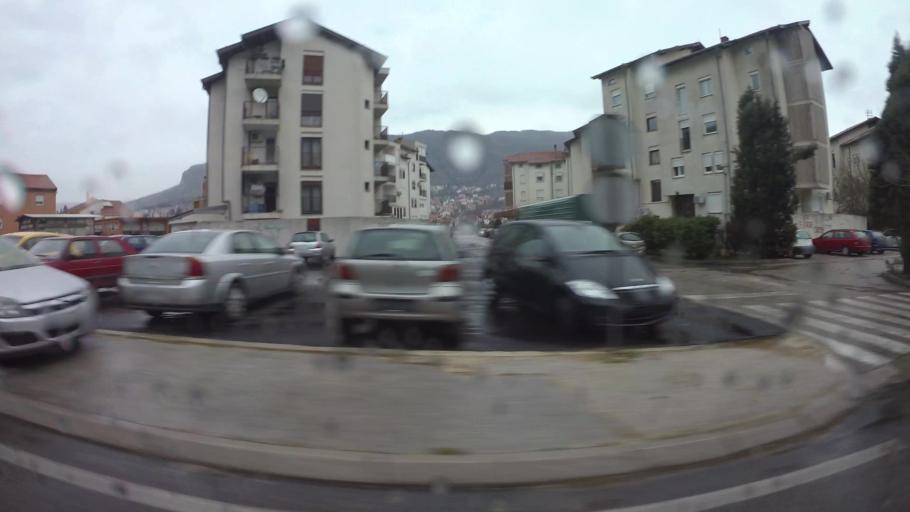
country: BA
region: Federation of Bosnia and Herzegovina
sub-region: Hercegovacko-Bosanski Kanton
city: Mostar
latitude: 43.3271
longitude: 17.8168
